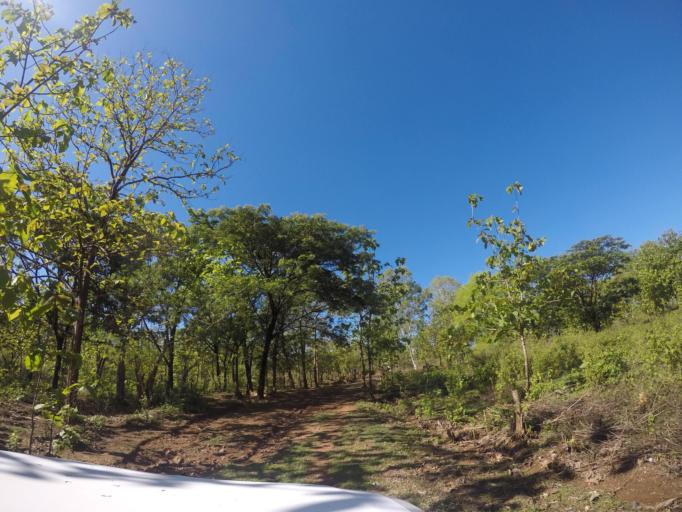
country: TL
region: Bobonaro
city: Maliana
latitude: -8.9983
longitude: 125.2048
